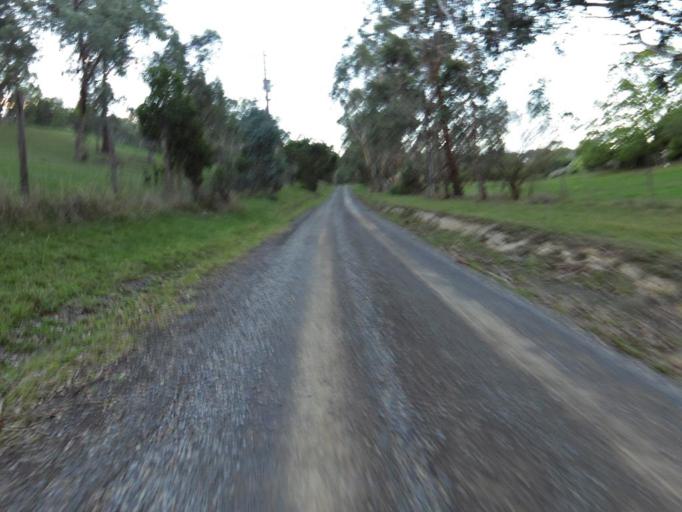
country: AU
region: Victoria
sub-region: Manningham
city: Warrandyte
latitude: -37.7421
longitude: 145.2375
